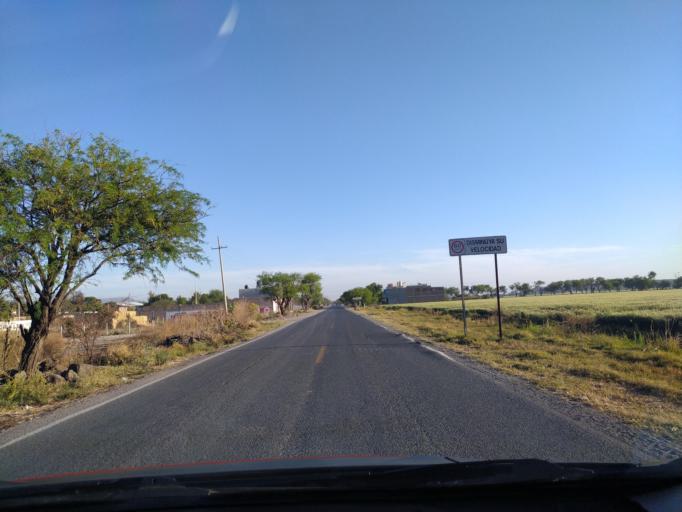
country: MX
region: Guanajuato
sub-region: San Francisco del Rincon
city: San Ignacio de Hidalgo
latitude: 20.9078
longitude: -101.8577
